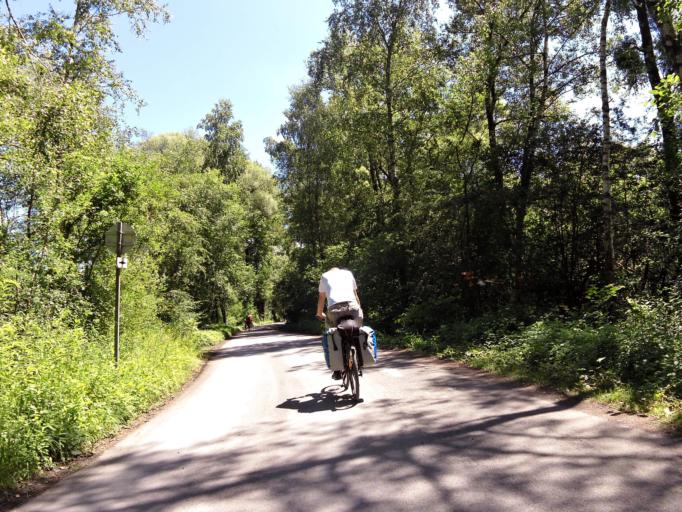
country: AT
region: Vorarlberg
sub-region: Politischer Bezirk Bregenz
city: Fussach
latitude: 47.4905
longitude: 9.6664
